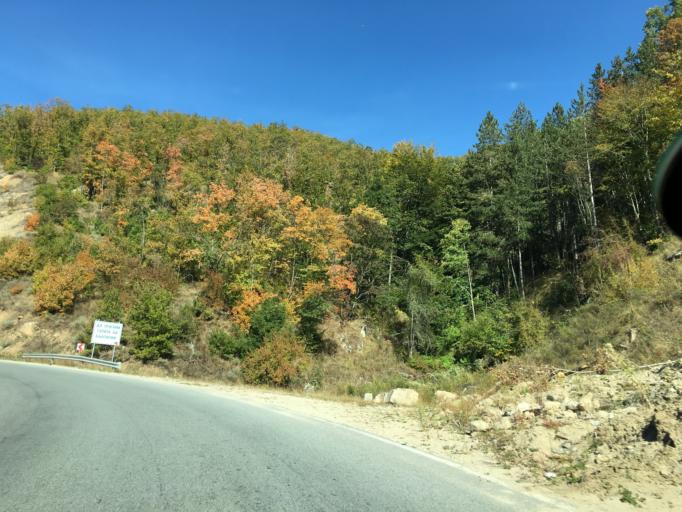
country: BG
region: Smolyan
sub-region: Obshtina Devin
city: Devin
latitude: 41.7683
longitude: 24.4519
